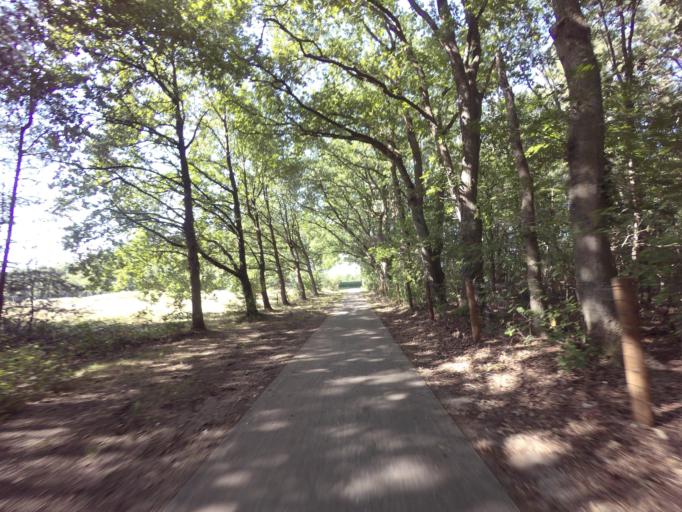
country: NL
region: Gelderland
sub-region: Gemeente Apeldoorn
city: Loenen
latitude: 52.1494
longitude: 6.0269
